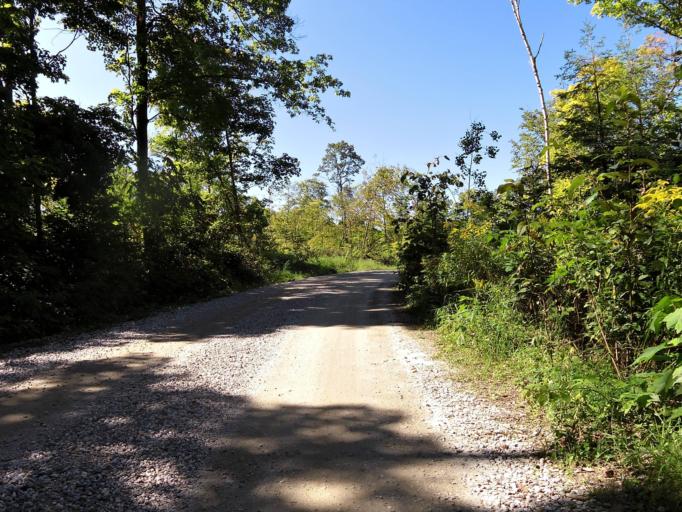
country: CA
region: Ontario
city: Renfrew
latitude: 45.1298
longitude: -76.7200
